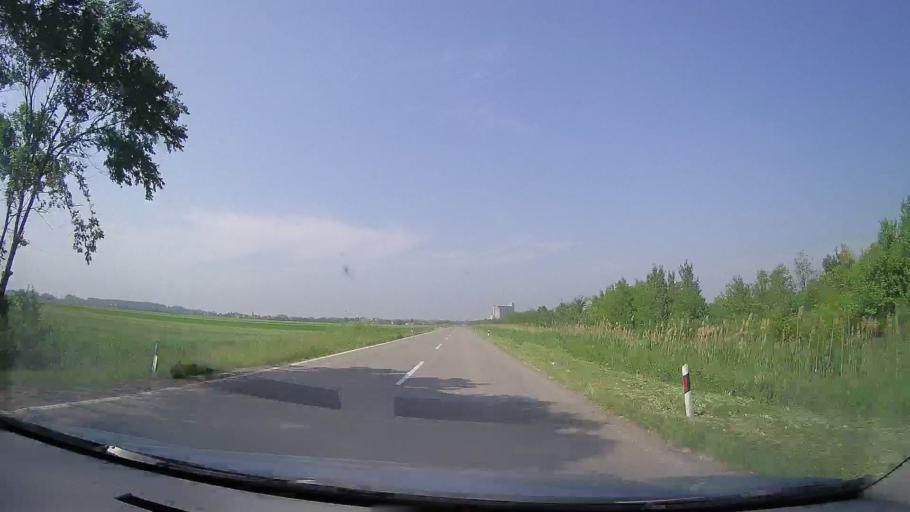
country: RS
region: Autonomna Pokrajina Vojvodina
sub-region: Srednjebanatski Okrug
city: Secanj
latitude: 45.3800
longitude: 20.7866
